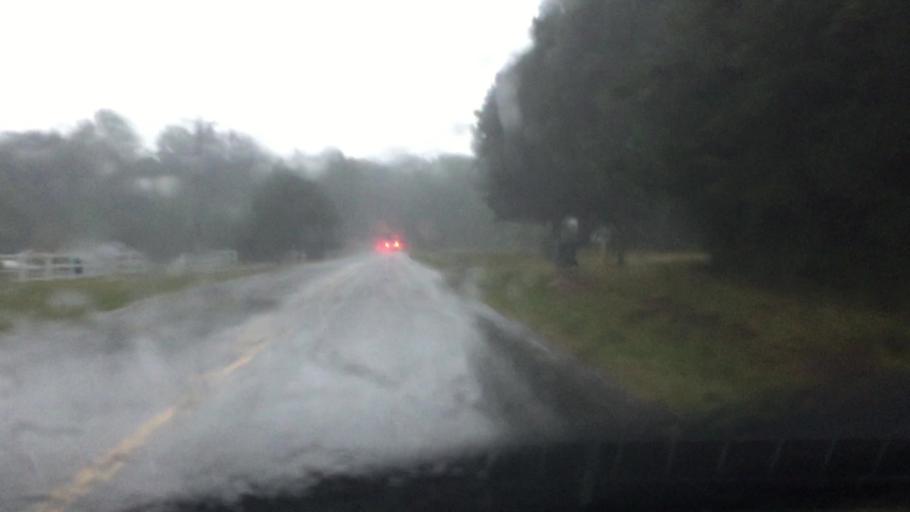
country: US
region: North Carolina
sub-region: Gaston County
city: Davidson
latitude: 35.4929
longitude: -80.7675
